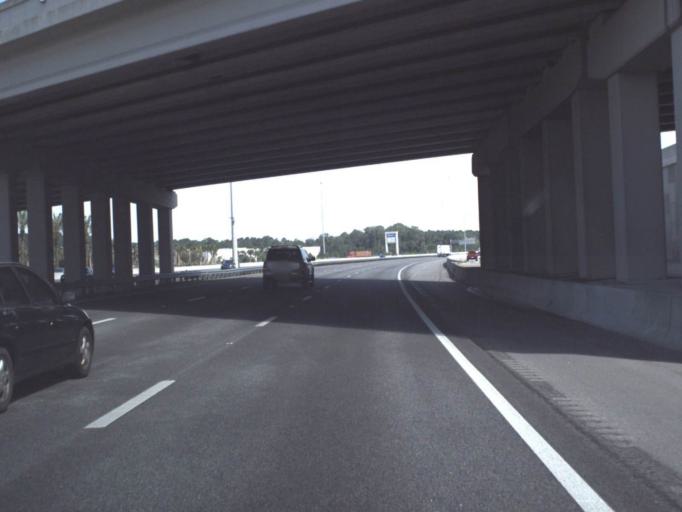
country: US
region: Florida
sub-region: Clay County
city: Bellair-Meadowbrook Terrace
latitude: 30.2040
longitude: -81.7550
